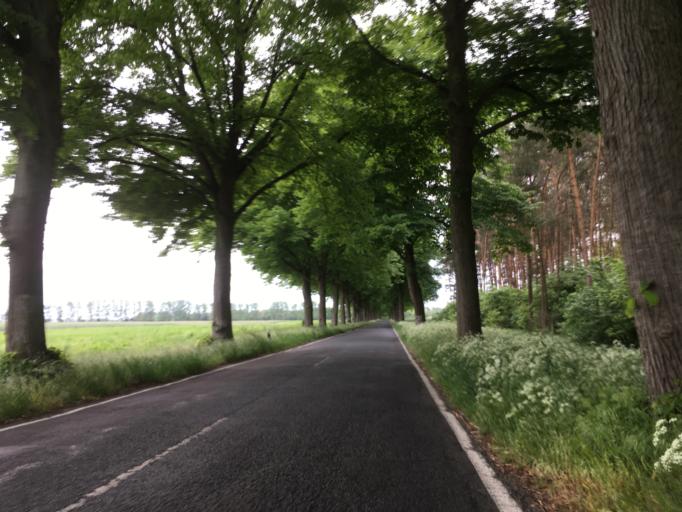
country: DE
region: Brandenburg
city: Werneuchen
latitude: 52.6760
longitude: 13.7152
